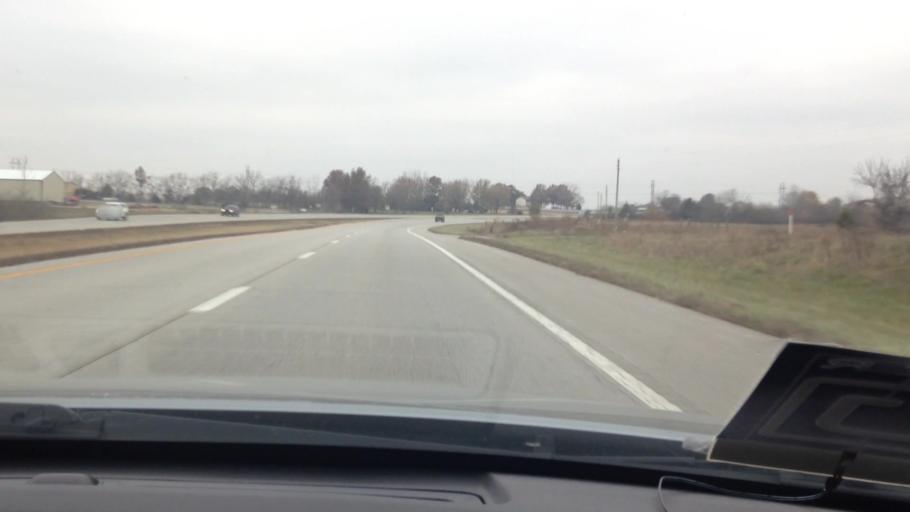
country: US
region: Missouri
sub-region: Cass County
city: Harrisonville
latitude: 38.6099
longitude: -94.3170
